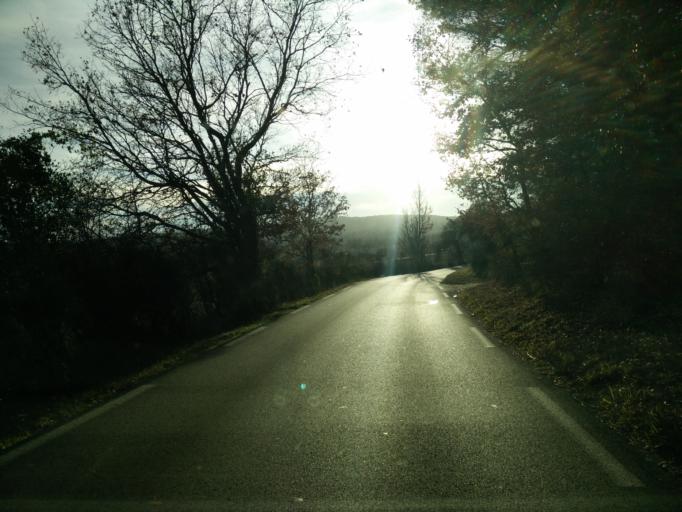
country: FR
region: Provence-Alpes-Cote d'Azur
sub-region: Departement du Var
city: Callian
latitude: 43.6117
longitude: 6.7376
